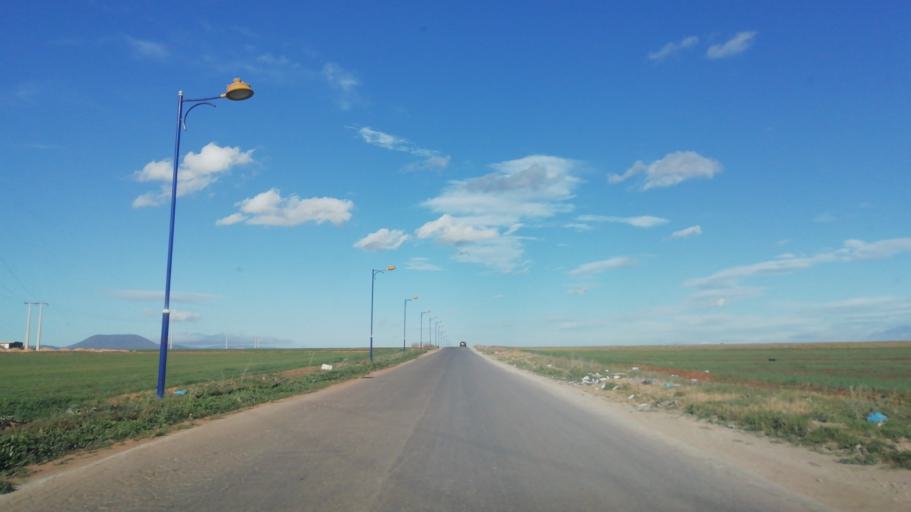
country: DZ
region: Oran
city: Sidi ech Chahmi
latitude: 35.6433
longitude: -0.5367
